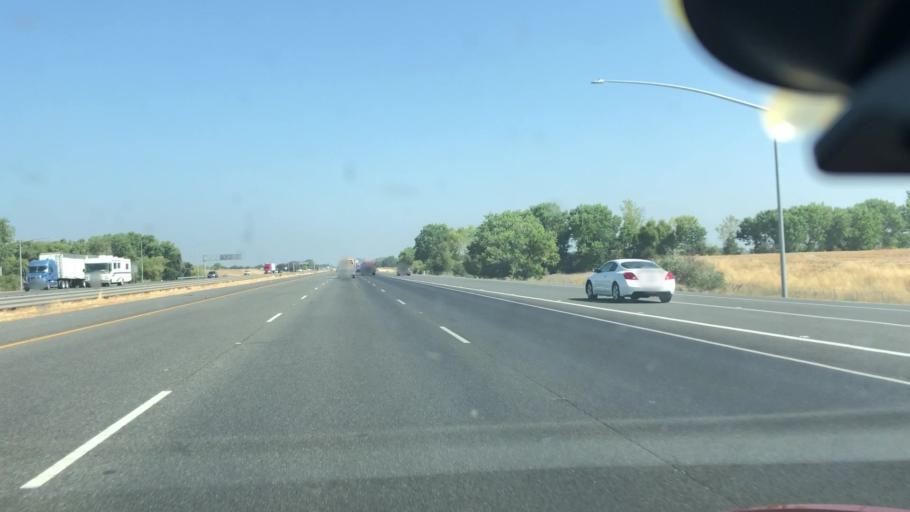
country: US
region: California
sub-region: Sacramento County
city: Laguna
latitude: 38.4291
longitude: -121.4878
